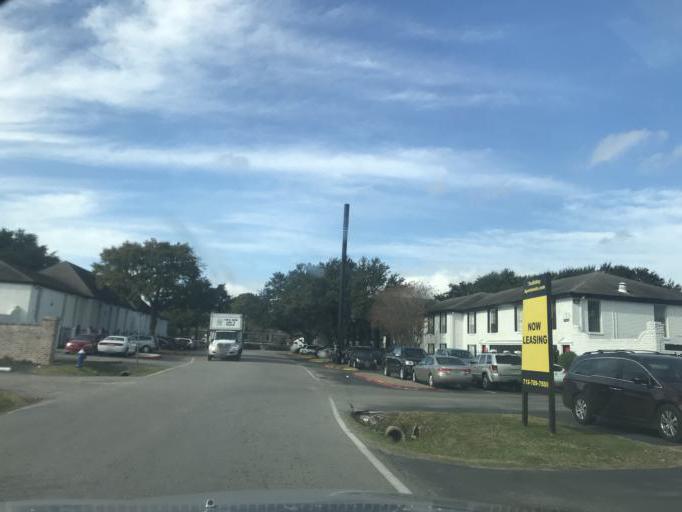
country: US
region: Texas
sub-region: Harris County
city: Hunters Creek Village
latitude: 29.7354
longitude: -95.4884
